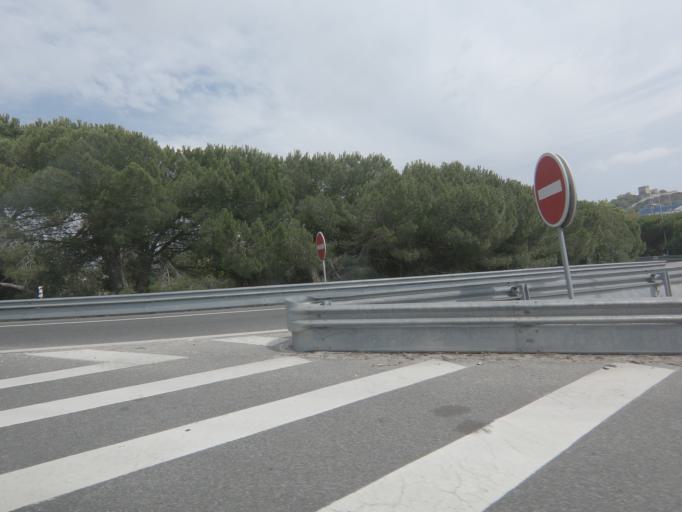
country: PT
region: Leiria
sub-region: Leiria
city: Leiria
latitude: 39.7537
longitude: -8.8163
